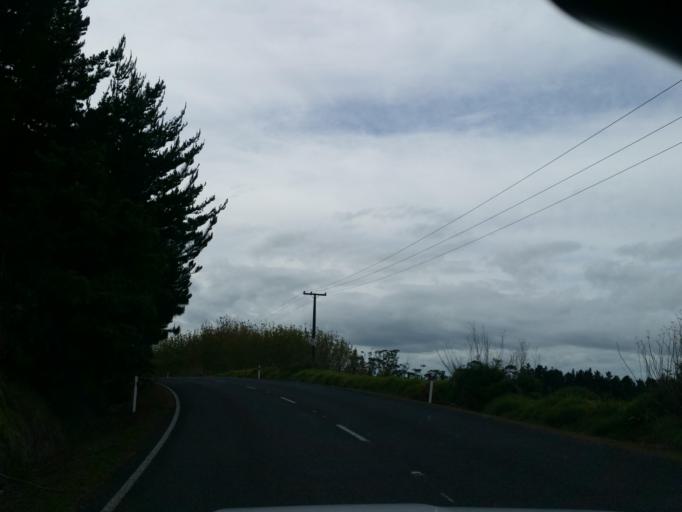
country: NZ
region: Northland
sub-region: Kaipara District
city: Dargaville
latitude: -35.9539
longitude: 173.9222
